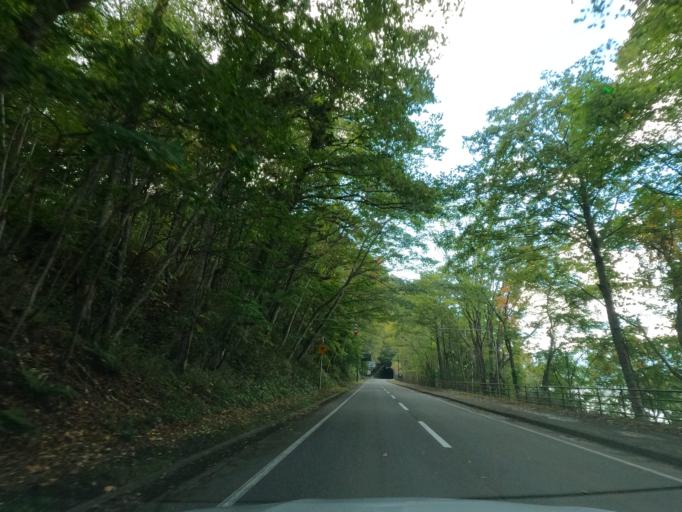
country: JP
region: Hokkaido
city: Shiraoi
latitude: 42.7044
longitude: 141.2937
